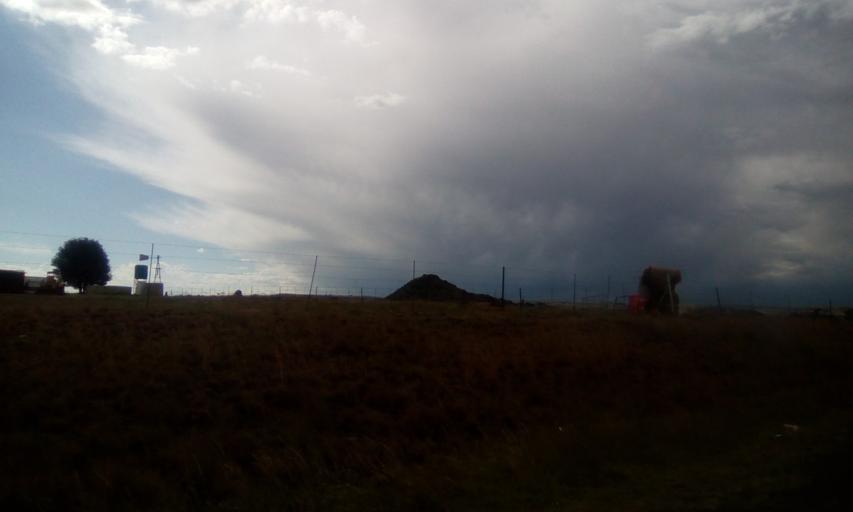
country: ZA
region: Orange Free State
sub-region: Thabo Mofutsanyana District Municipality
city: Ladybrand
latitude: -29.2630
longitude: 27.4338
